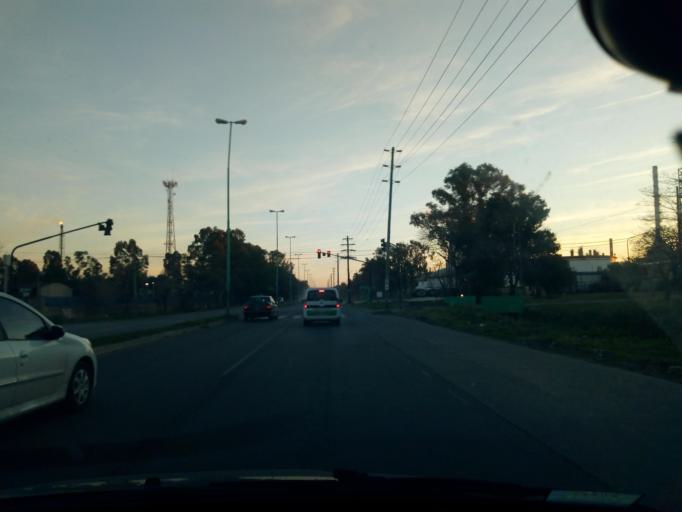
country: AR
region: Buenos Aires
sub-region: Partido de Ensenada
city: Ensenada
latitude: -34.8754
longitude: -57.9173
